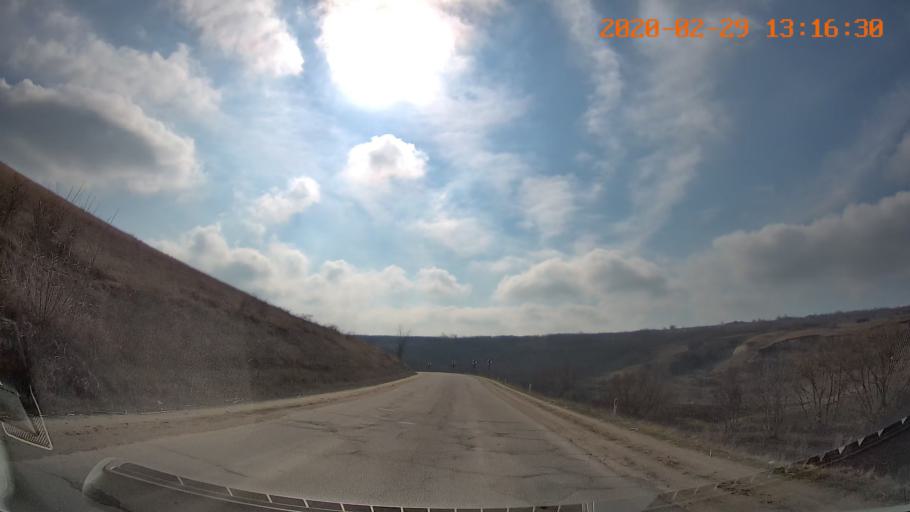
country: MD
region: Telenesti
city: Camenca
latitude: 48.0021
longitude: 28.6633
